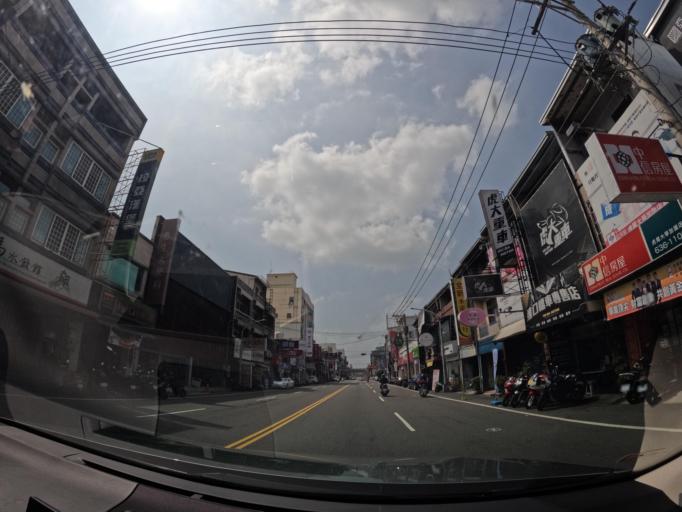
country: TW
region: Taiwan
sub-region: Yunlin
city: Douliu
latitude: 23.7049
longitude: 120.4289
